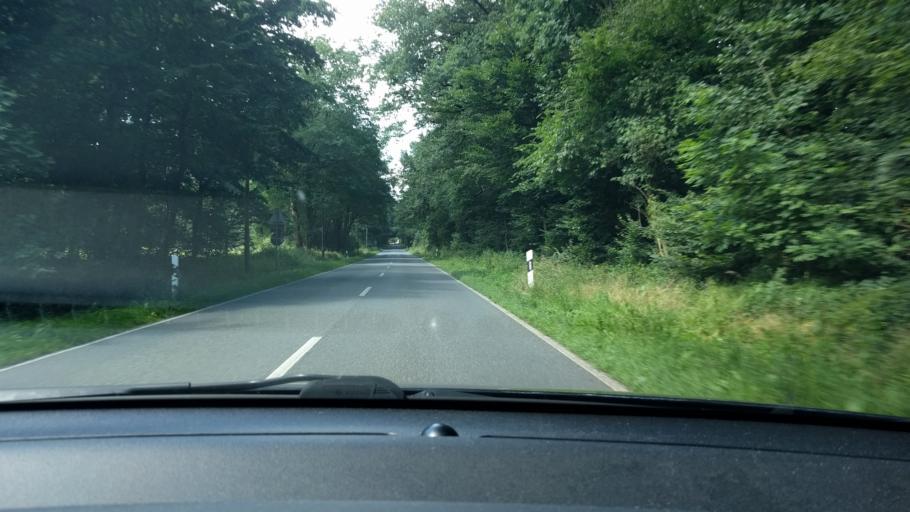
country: DE
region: North Rhine-Westphalia
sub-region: Regierungsbezirk Munster
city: Haltern
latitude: 51.7277
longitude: 7.2437
